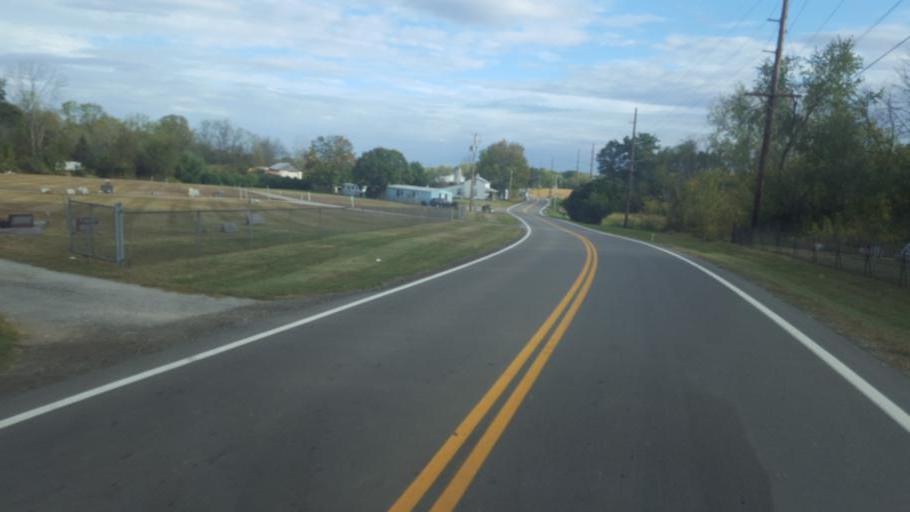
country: US
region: Ohio
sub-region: Ashland County
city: Ashland
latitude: 40.8006
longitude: -82.1943
